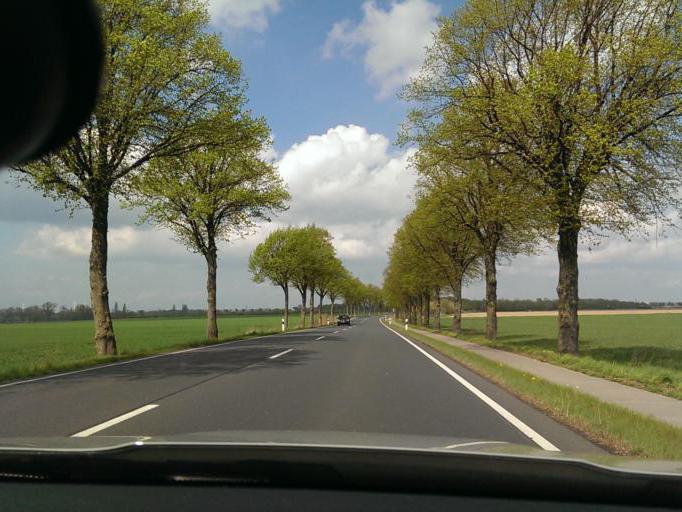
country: DE
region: Lower Saxony
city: Pattensen
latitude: 52.2377
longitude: 9.7561
